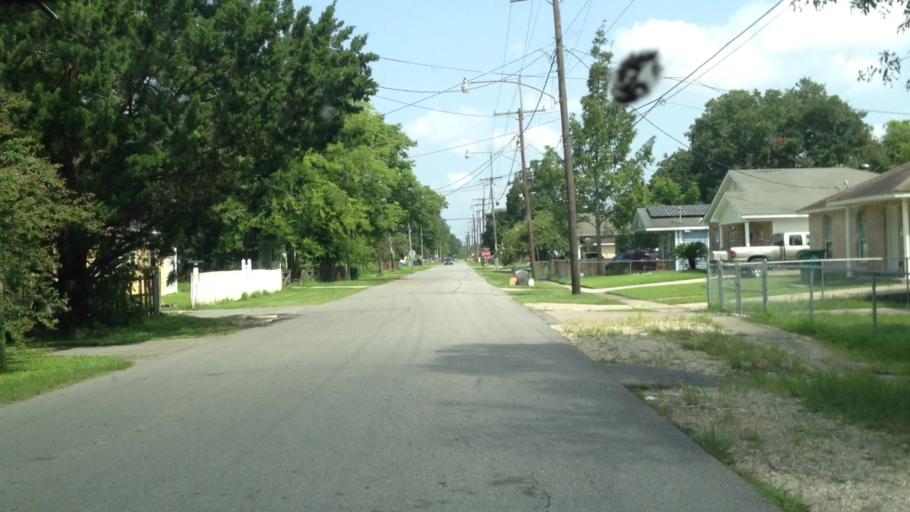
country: US
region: Louisiana
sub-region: Jefferson Parish
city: Bridge City
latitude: 29.9308
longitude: -90.1676
